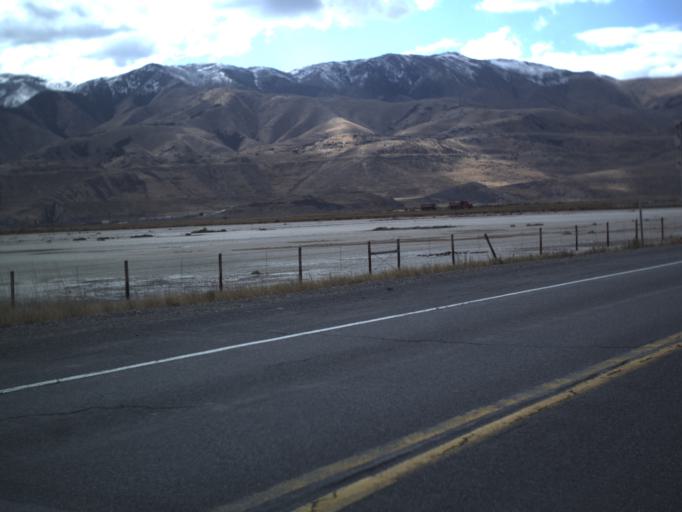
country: US
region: Utah
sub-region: Tooele County
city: Grantsville
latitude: 40.7052
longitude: -112.5252
